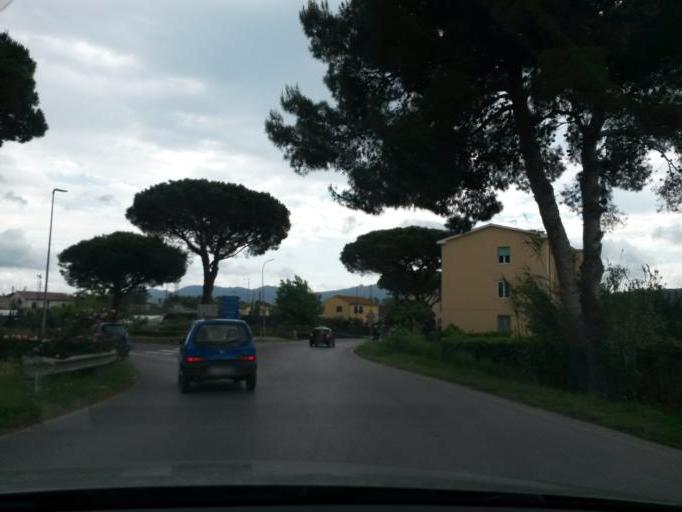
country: IT
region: Tuscany
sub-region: Provincia di Livorno
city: Portoferraio
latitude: 42.8023
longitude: 10.3081
